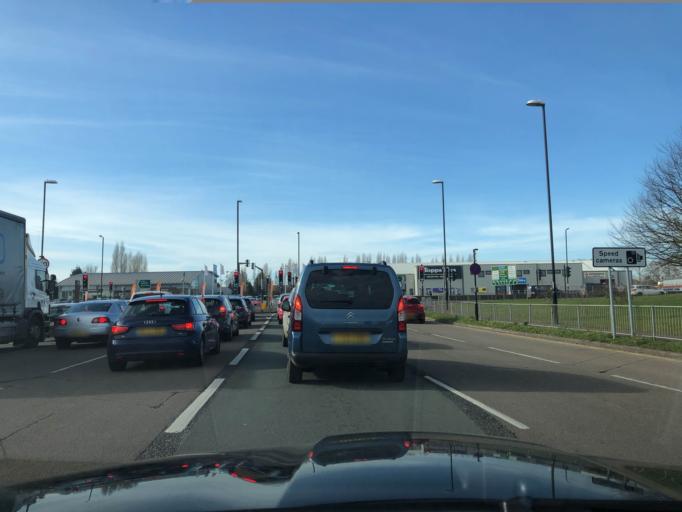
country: GB
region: England
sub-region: Coventry
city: Coventry
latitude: 52.4024
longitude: -1.5576
